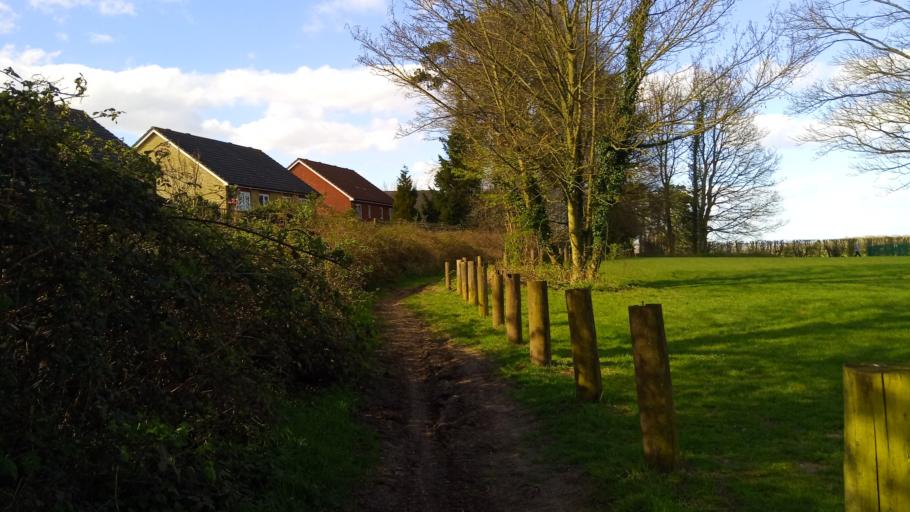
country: GB
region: England
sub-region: Kent
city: Chartham
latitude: 51.2456
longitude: 1.0335
